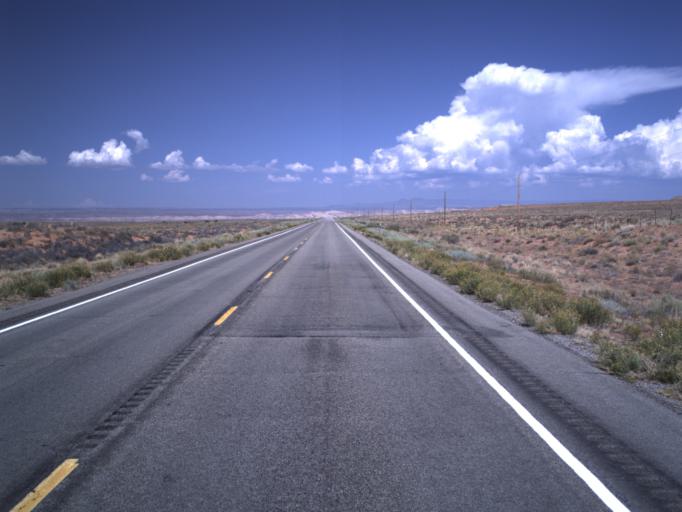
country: US
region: Utah
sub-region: San Juan County
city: Blanding
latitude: 37.1376
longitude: -109.5561
